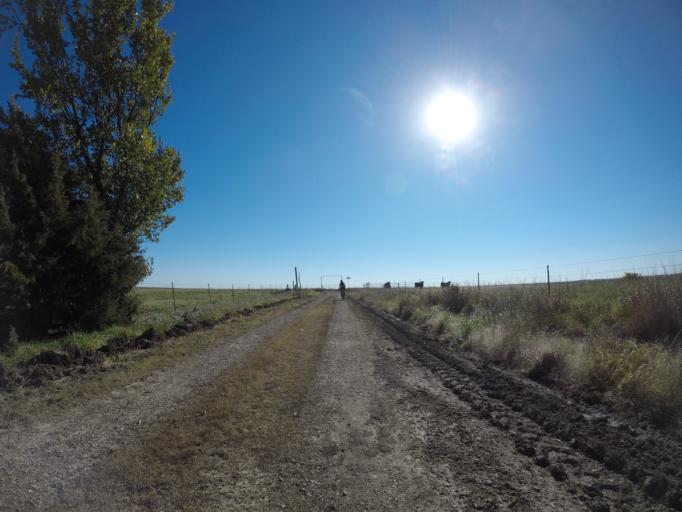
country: US
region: Kansas
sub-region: Wabaunsee County
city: Alma
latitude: 38.8817
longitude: -96.3675
